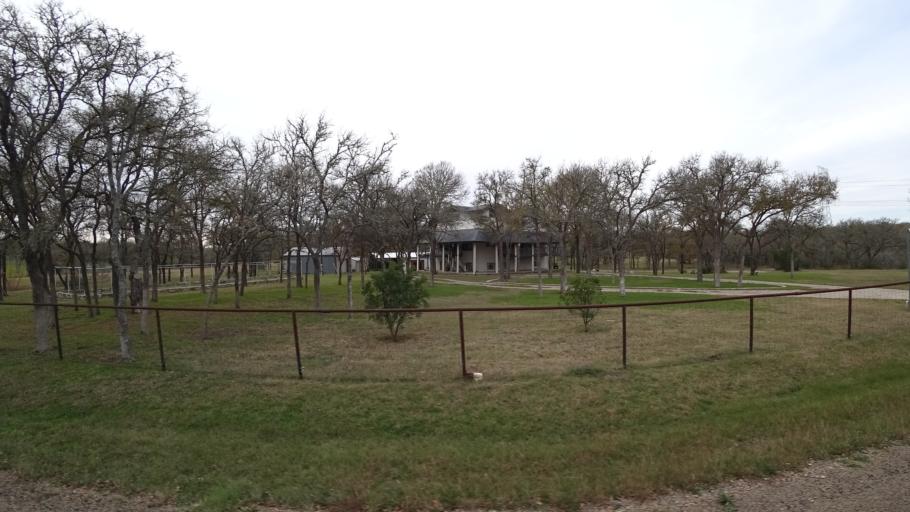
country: US
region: Texas
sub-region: Travis County
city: Garfield
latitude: 30.1093
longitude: -97.5624
